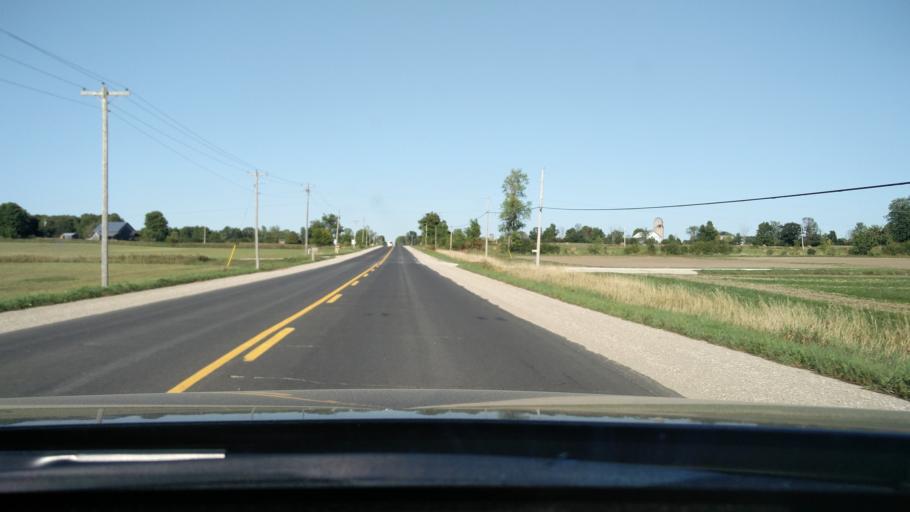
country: CA
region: Ontario
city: Perth
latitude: 44.8661
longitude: -76.2820
